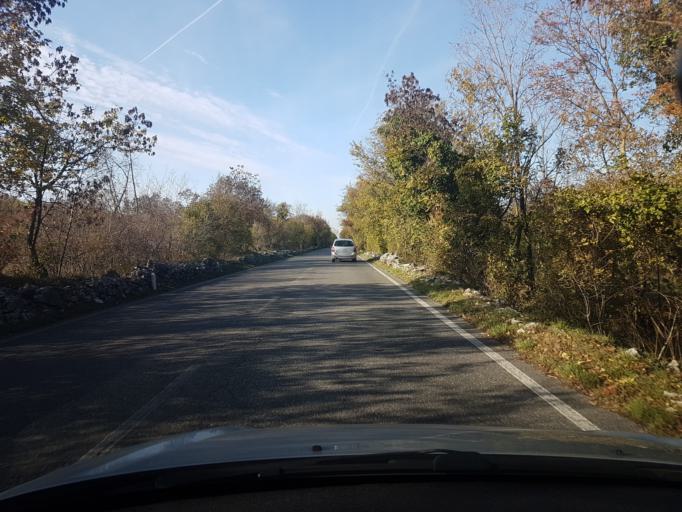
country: IT
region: Friuli Venezia Giulia
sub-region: Provincia di Trieste
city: Santa Croce
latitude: 45.7281
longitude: 13.7084
